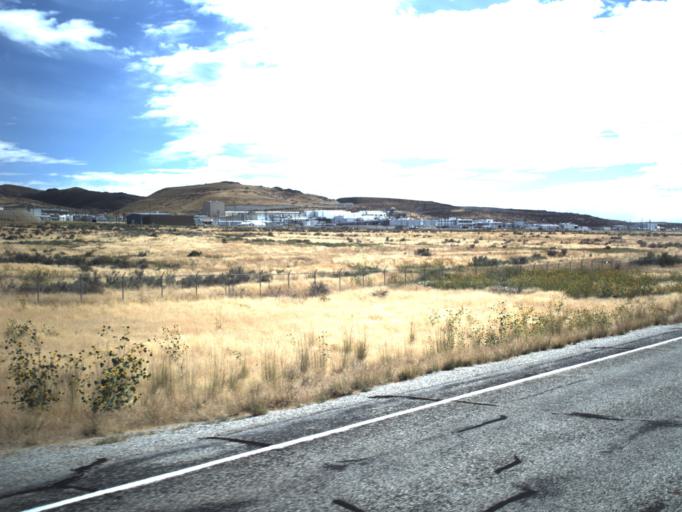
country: US
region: Utah
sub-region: Box Elder County
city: Tremonton
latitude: 41.6689
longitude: -112.4463
